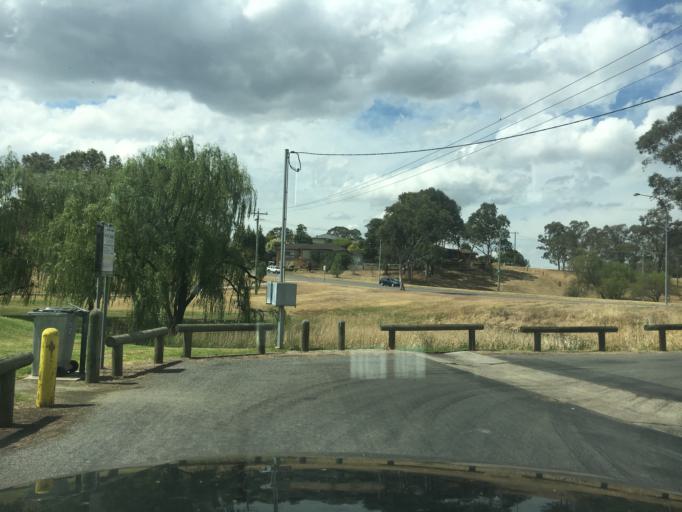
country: AU
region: New South Wales
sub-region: Singleton
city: Singleton
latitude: -32.5476
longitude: 151.1694
